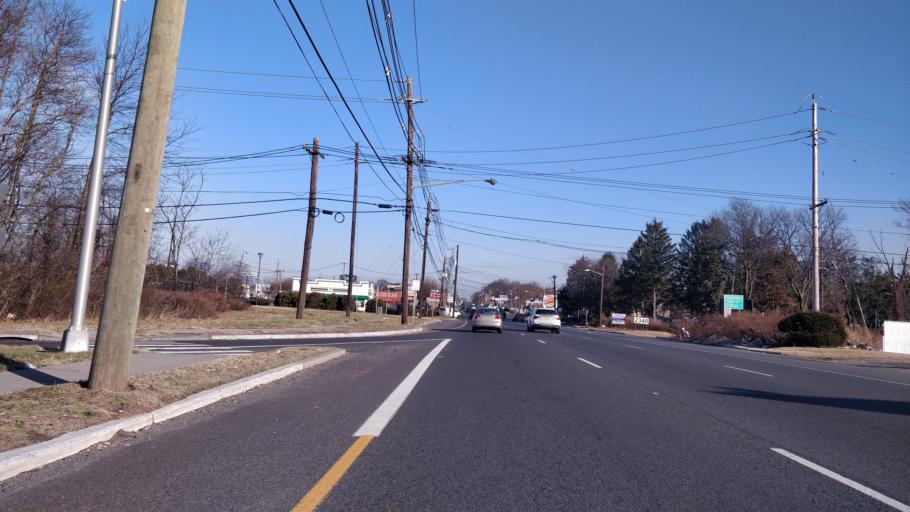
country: US
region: New Jersey
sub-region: Union County
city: Kenilworth
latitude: 40.6902
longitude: -74.2935
